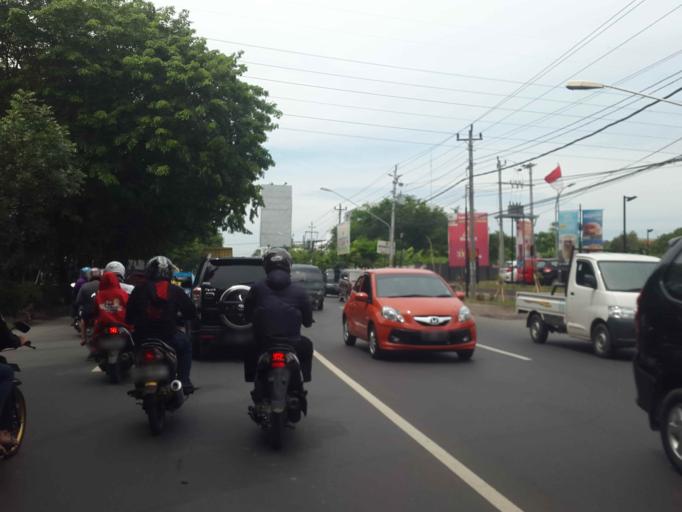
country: ID
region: Central Java
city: Semarang
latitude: -7.0089
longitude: 110.4652
